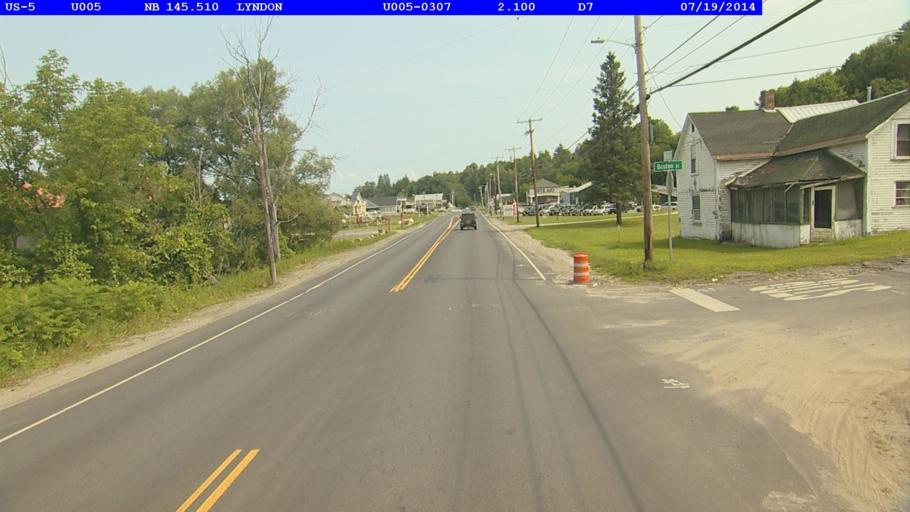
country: US
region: Vermont
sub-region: Caledonia County
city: Lyndonville
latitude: 44.5237
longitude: -72.0013
